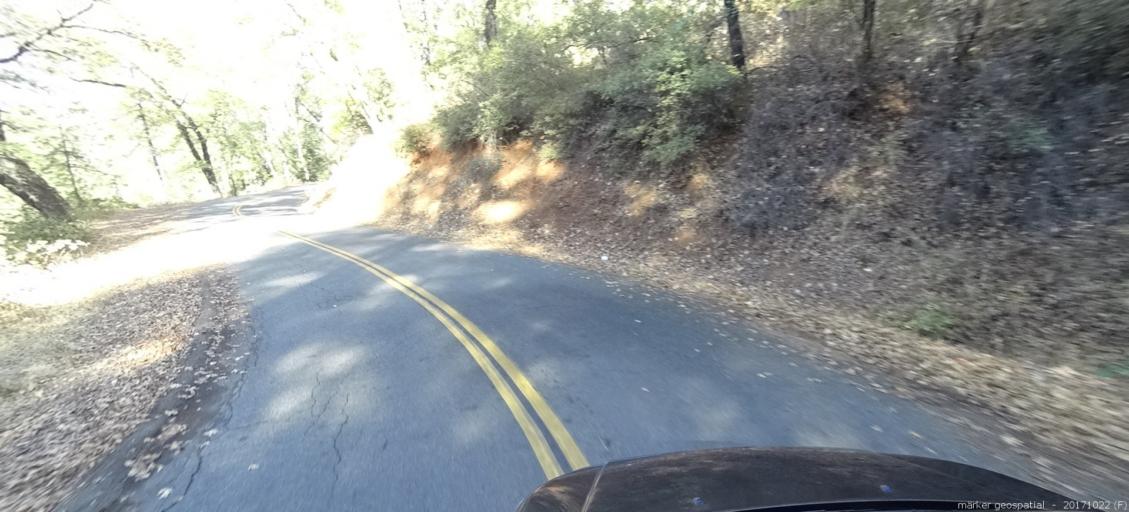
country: US
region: California
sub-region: Shasta County
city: Shasta Lake
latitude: 40.8450
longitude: -122.3477
